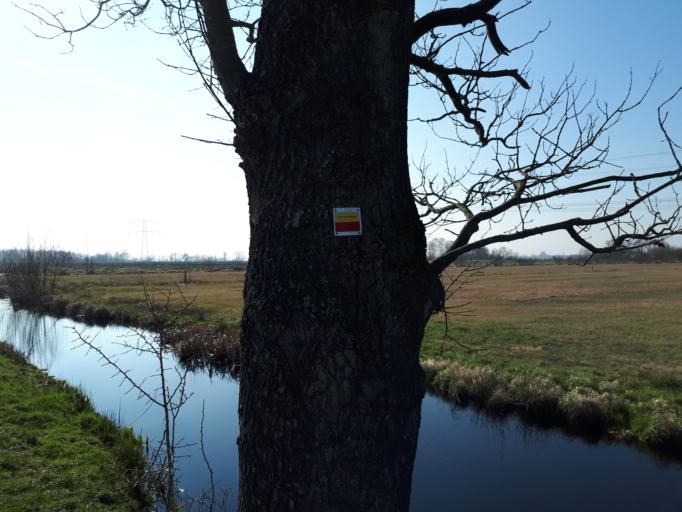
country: NL
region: South Holland
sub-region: Molenwaard
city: Nieuw-Lekkerland
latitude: 51.9491
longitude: 4.6860
